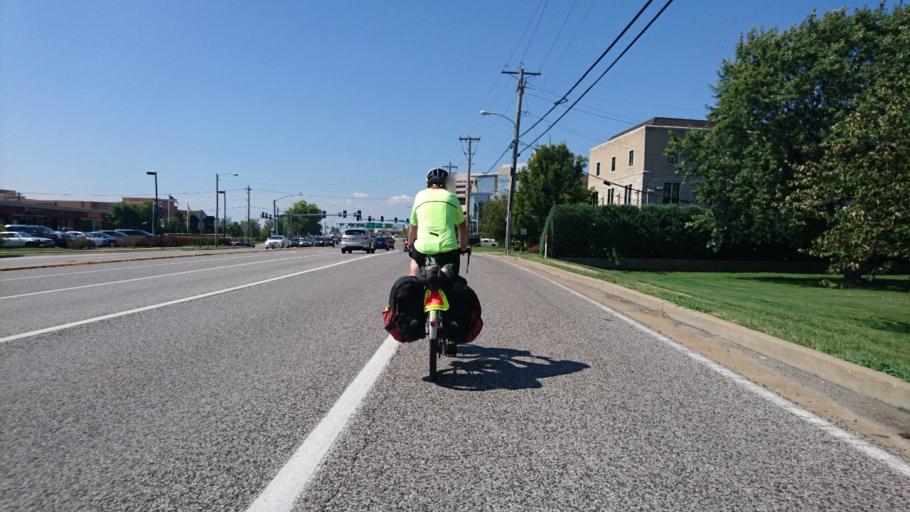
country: US
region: Missouri
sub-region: Saint Louis County
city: Des Peres
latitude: 38.6036
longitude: -90.4427
